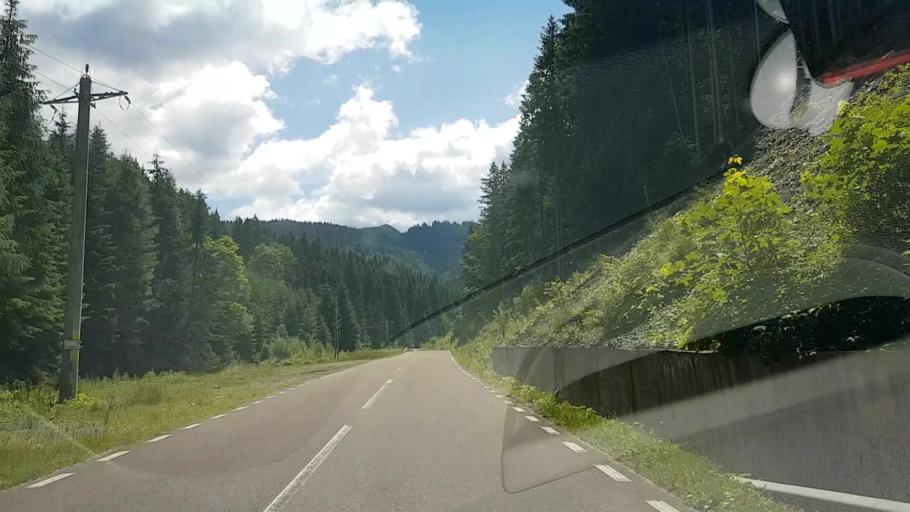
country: RO
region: Suceava
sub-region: Comuna Sadova
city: Sadova
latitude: 47.4758
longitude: 25.4995
